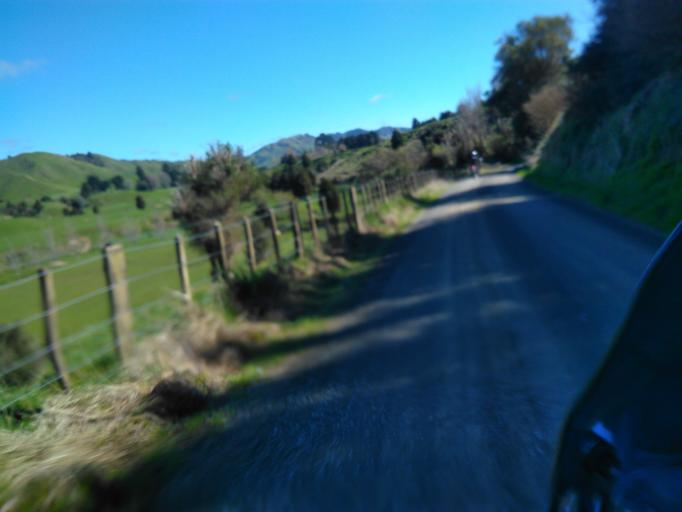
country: NZ
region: Bay of Plenty
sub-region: Opotiki District
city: Opotiki
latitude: -38.3001
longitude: 177.5575
